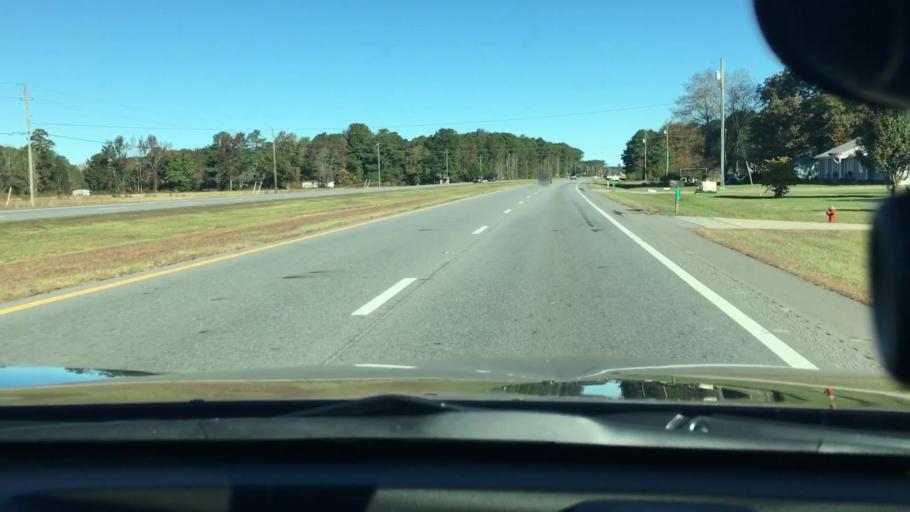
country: US
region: North Carolina
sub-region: Pitt County
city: Greenville
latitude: 35.6859
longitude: -77.3657
